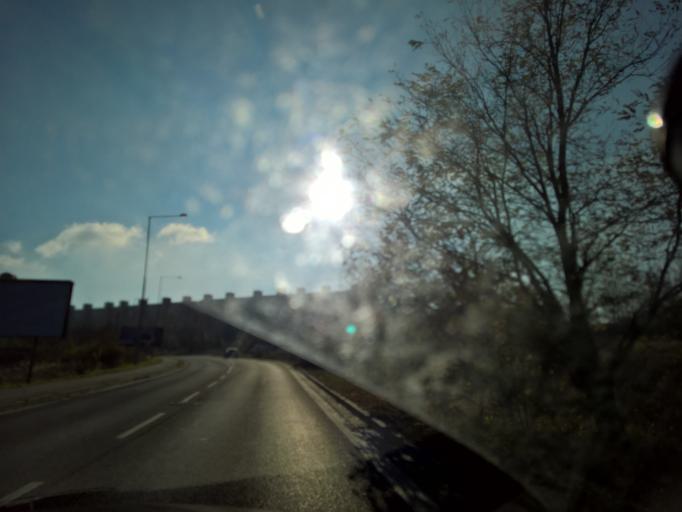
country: SK
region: Nitriansky
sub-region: Okres Nitra
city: Nitra
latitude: 48.3100
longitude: 18.0490
